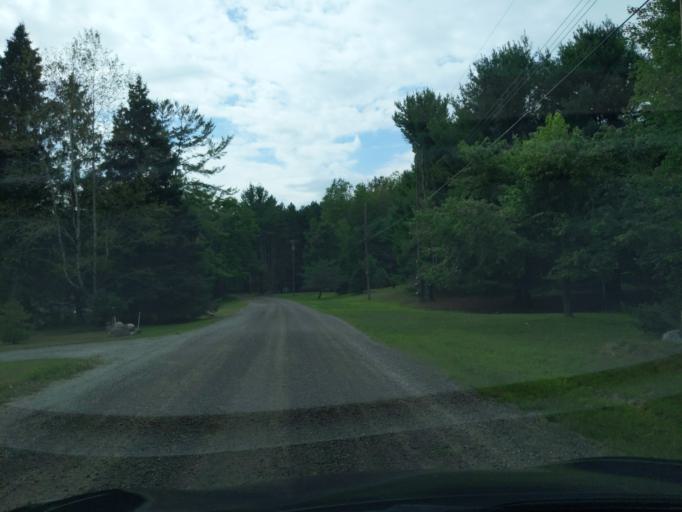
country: US
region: Michigan
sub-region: Clare County
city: Harrison
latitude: 43.9779
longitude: -85.0007
